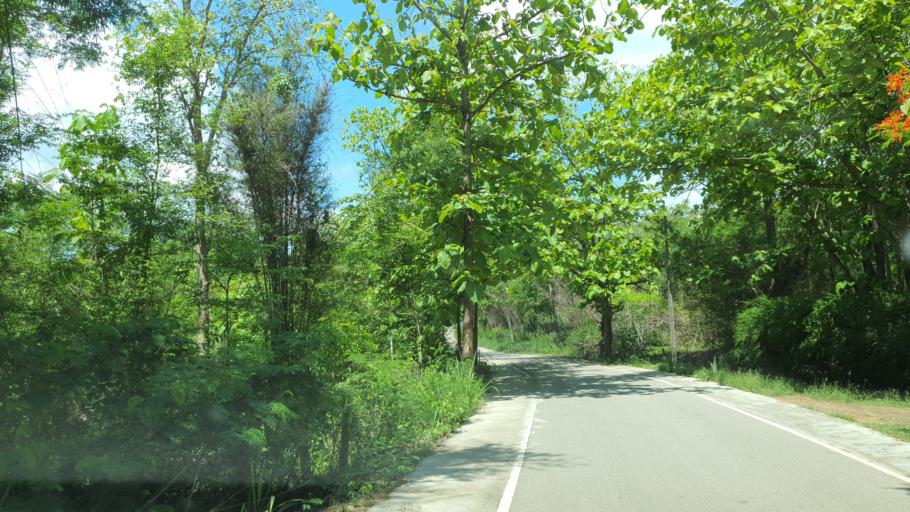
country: TH
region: Chiang Mai
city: Mae On
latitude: 18.7956
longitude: 99.2489
